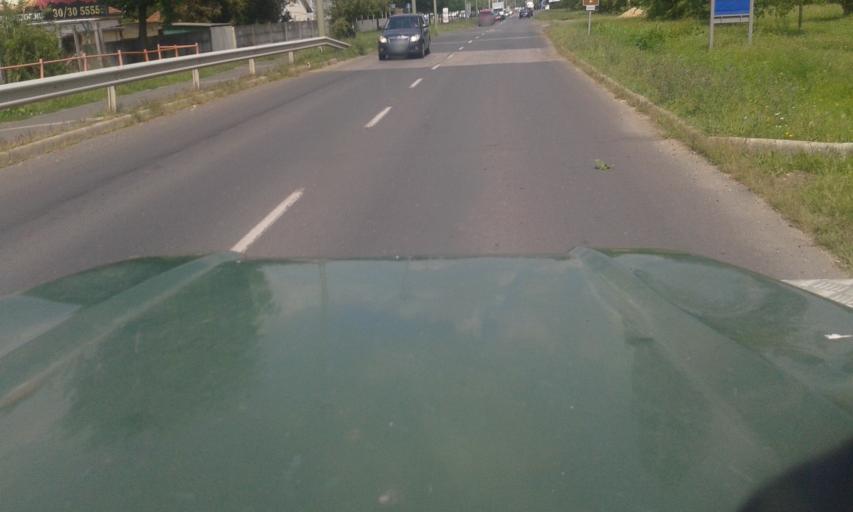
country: HU
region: Csongrad
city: Szeged
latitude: 46.2499
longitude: 20.1223
